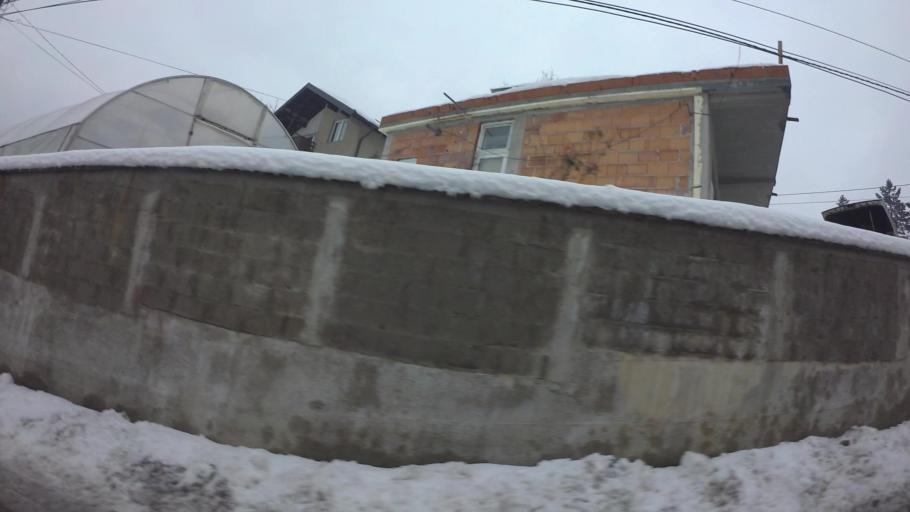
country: BA
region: Federation of Bosnia and Herzegovina
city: Hadzici
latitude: 43.8468
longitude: 18.2583
